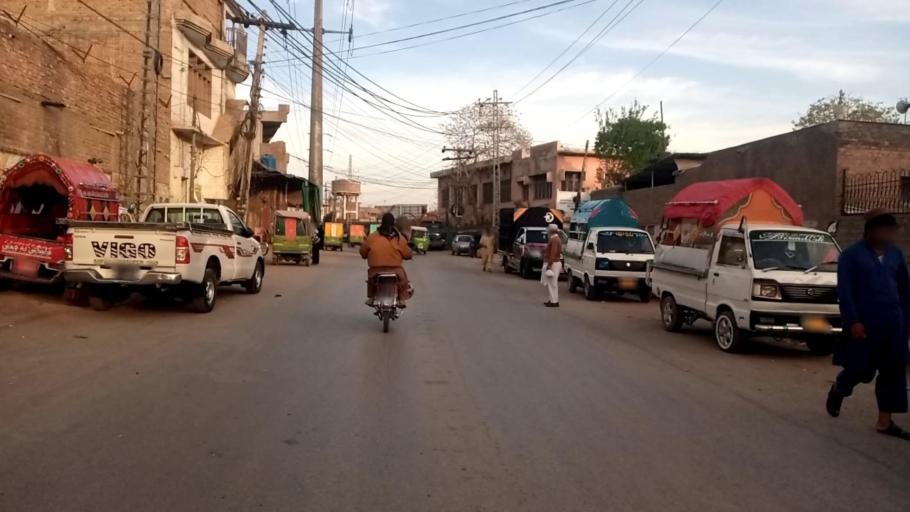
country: PK
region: Khyber Pakhtunkhwa
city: Peshawar
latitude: 34.0191
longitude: 71.5678
